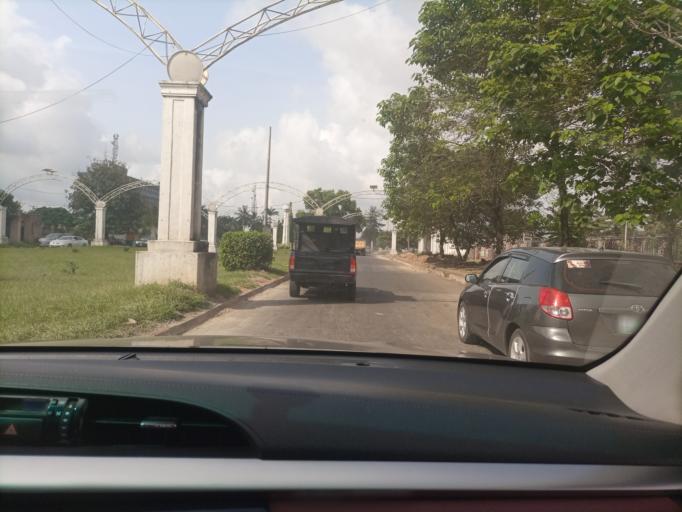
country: NG
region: Imo
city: Owerri
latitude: 5.4746
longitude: 7.0216
